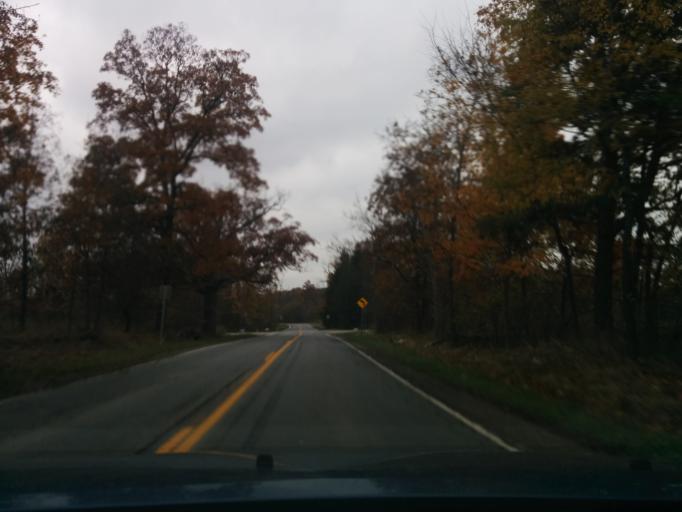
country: US
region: Michigan
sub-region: Washtenaw County
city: Dexter
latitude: 42.3860
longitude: -83.8419
